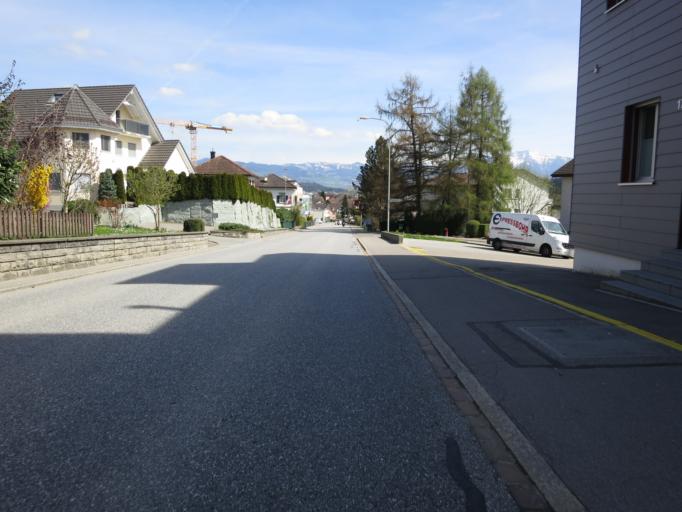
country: CH
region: Saint Gallen
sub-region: Wahlkreis See-Gaster
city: Eschenbach
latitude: 47.2412
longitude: 8.9179
